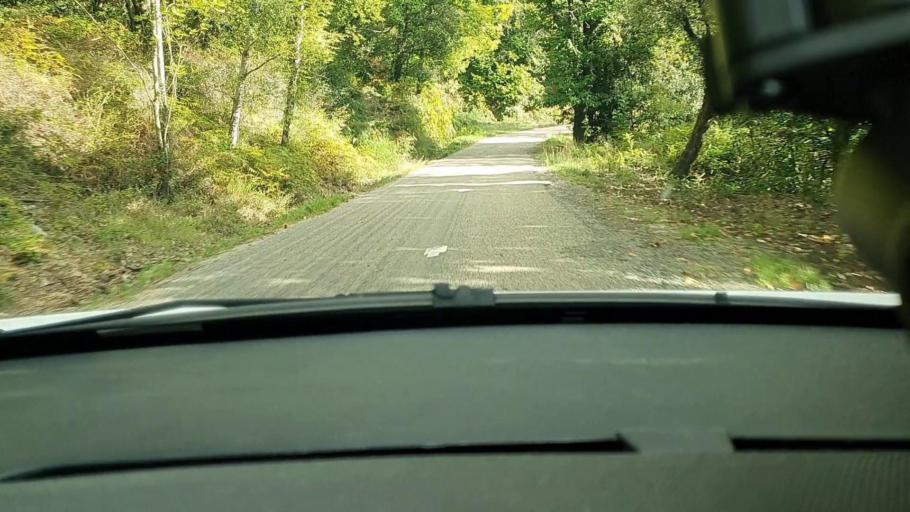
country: FR
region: Languedoc-Roussillon
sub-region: Departement du Gard
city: Besseges
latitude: 44.3547
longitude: 3.9891
